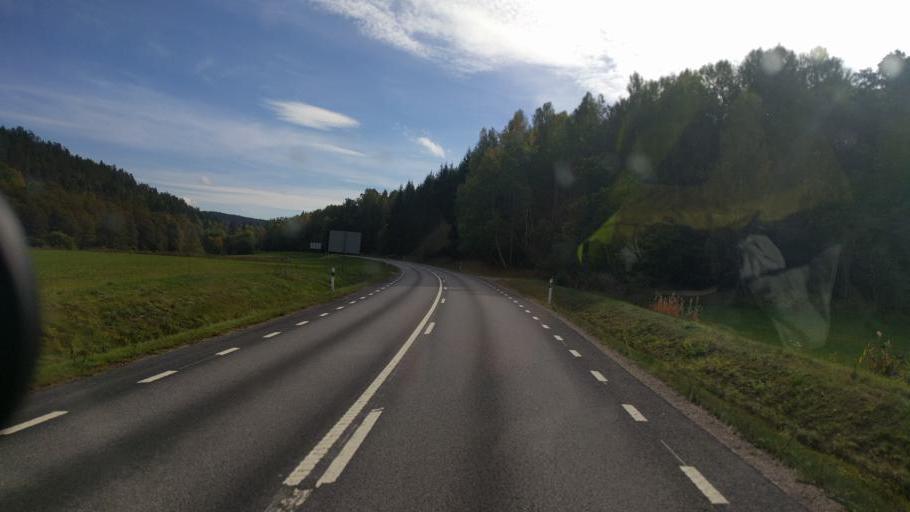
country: SE
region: OEstergoetland
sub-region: Kinda Kommun
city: Kisa
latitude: 57.9746
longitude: 15.6430
